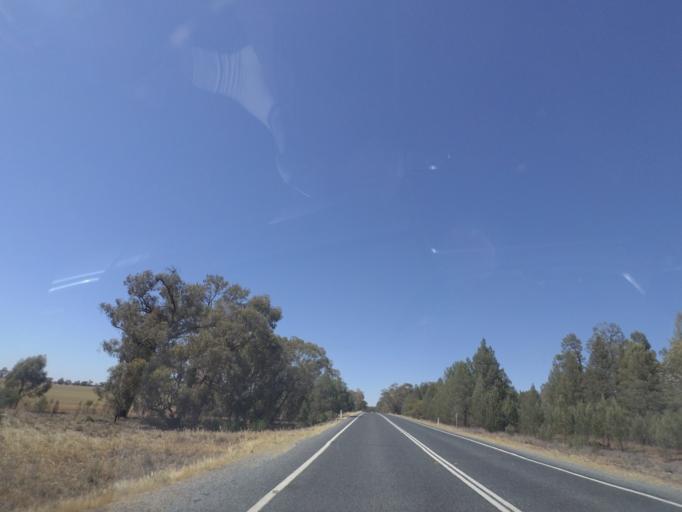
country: AU
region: New South Wales
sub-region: Narrandera
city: Narrandera
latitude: -34.4329
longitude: 146.8429
